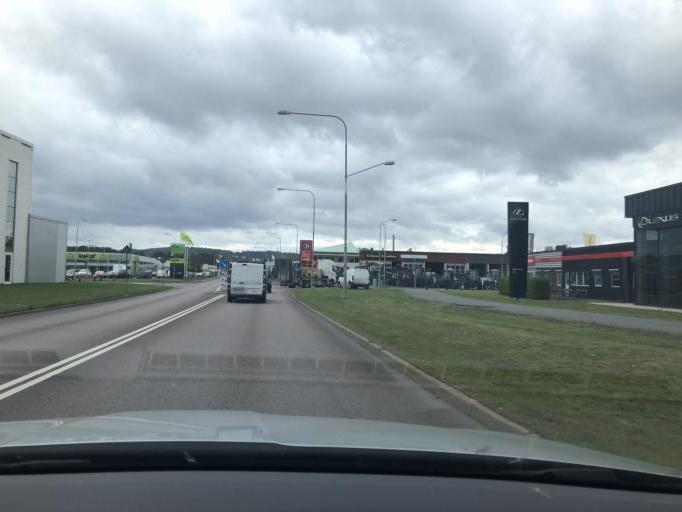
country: SE
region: Joenkoeping
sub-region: Jonkopings Kommun
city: Jonkoping
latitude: 57.7657
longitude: 14.1795
